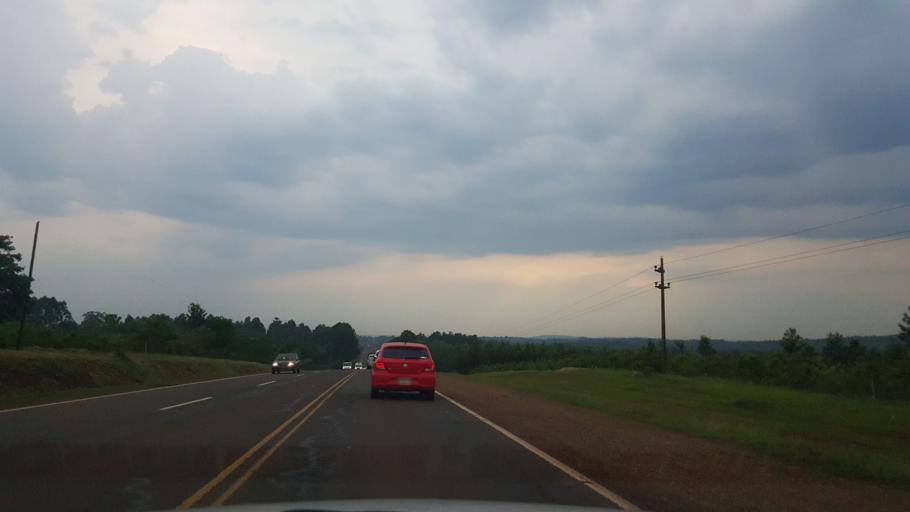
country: AR
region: Misiones
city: Gobernador Roca
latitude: -27.1651
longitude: -55.4391
